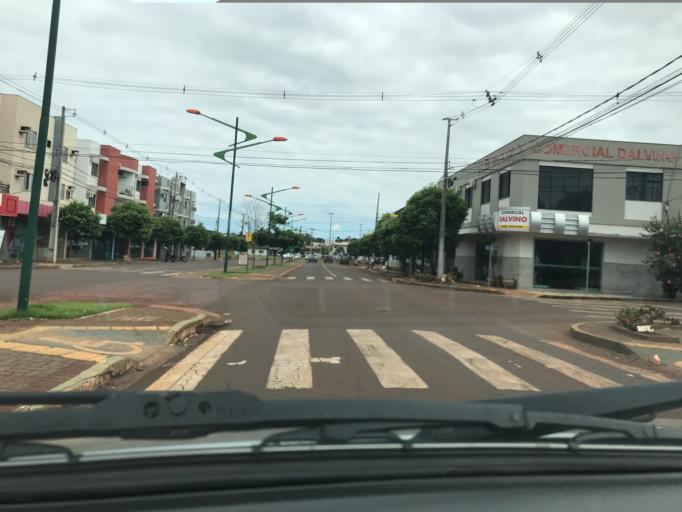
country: BR
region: Parana
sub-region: Palotina
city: Palotina
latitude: -24.2793
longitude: -53.8412
